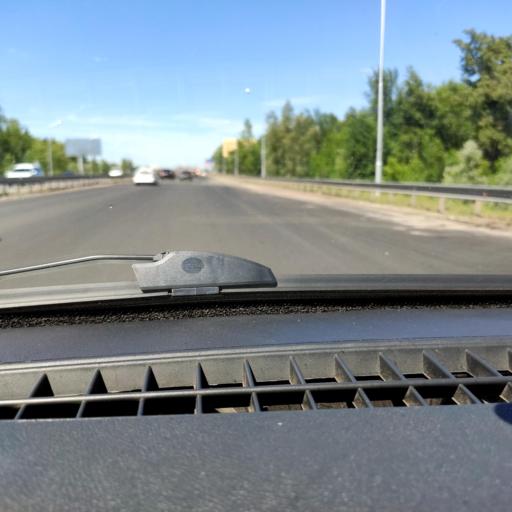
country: RU
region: Bashkortostan
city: Ufa
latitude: 54.6795
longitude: 56.0141
